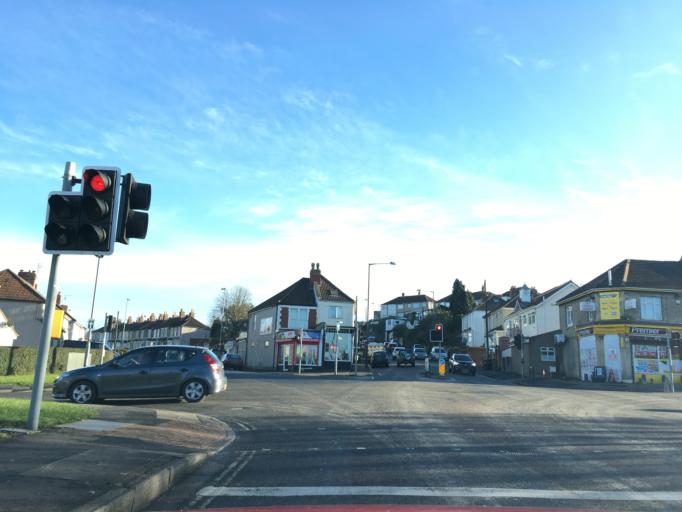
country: GB
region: England
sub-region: South Gloucestershire
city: Kingswood
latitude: 51.4708
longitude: -2.5206
